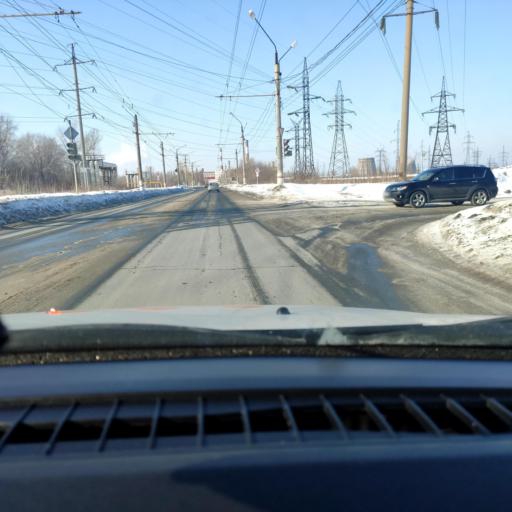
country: RU
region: Samara
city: Novokuybyshevsk
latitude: 53.1037
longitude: 49.9364
